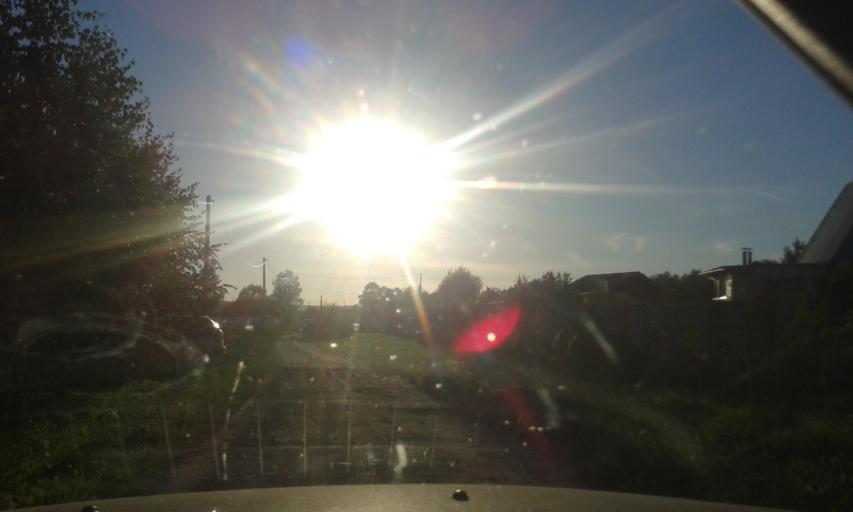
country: RU
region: Tula
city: Dubna
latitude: 54.1376
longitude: 37.1547
